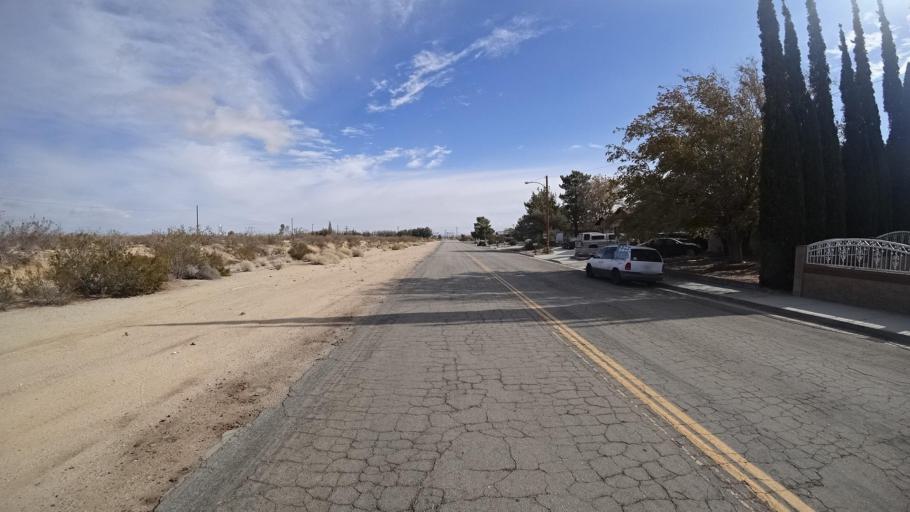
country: US
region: California
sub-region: Kern County
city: Mojave
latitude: 35.0685
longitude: -118.1830
